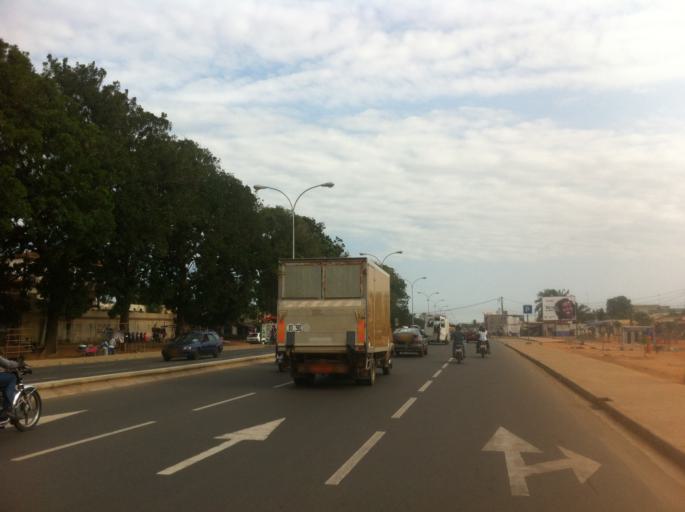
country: TG
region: Maritime
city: Lome
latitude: 6.1547
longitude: 1.2014
